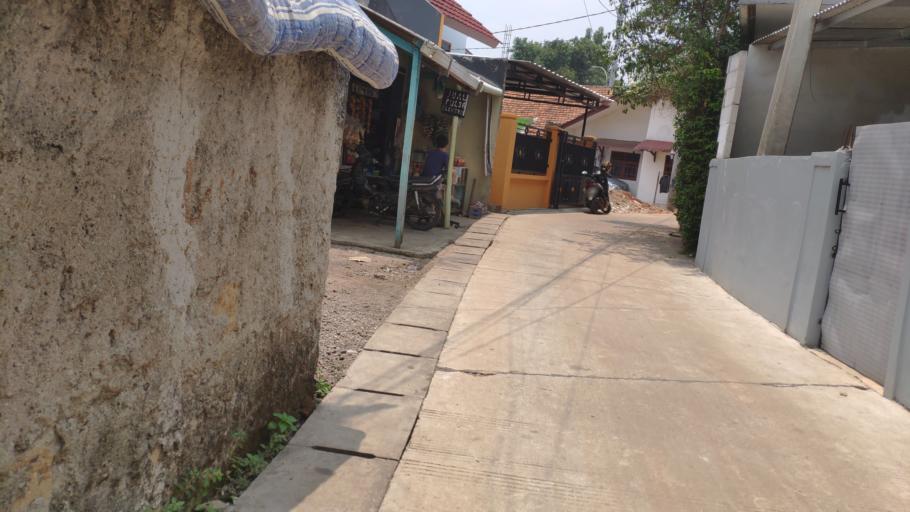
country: ID
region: West Java
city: Depok
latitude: -6.3516
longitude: 106.8051
